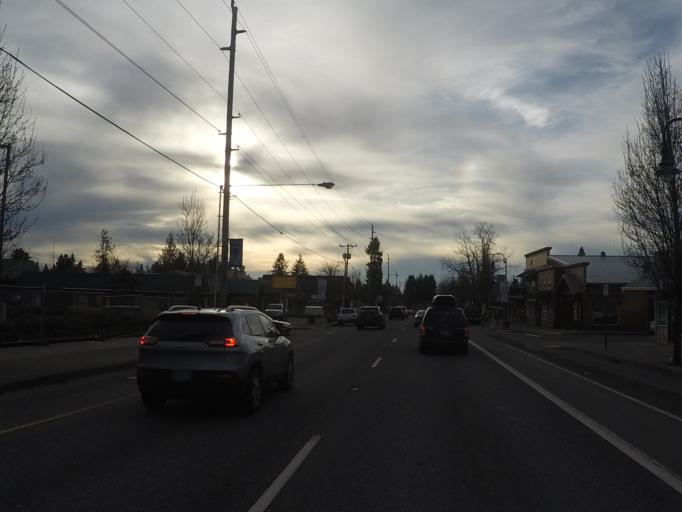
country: US
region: Oregon
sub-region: Clackamas County
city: Sandy
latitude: 45.3973
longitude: -122.2637
